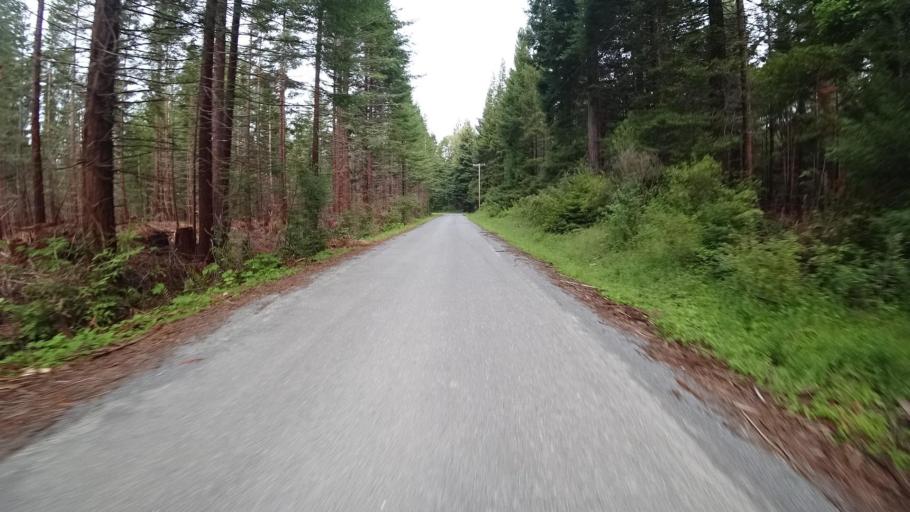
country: US
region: California
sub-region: Humboldt County
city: Redway
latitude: 40.3433
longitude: -123.8835
